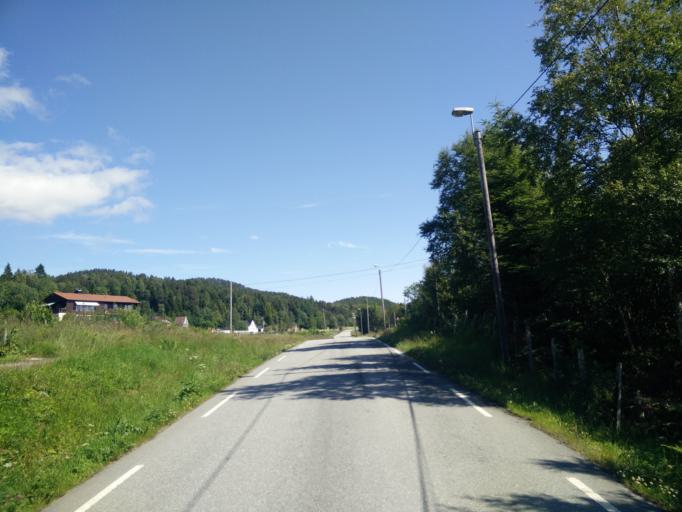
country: NO
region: More og Romsdal
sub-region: Kristiansund
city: Rensvik
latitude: 63.0347
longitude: 7.8222
